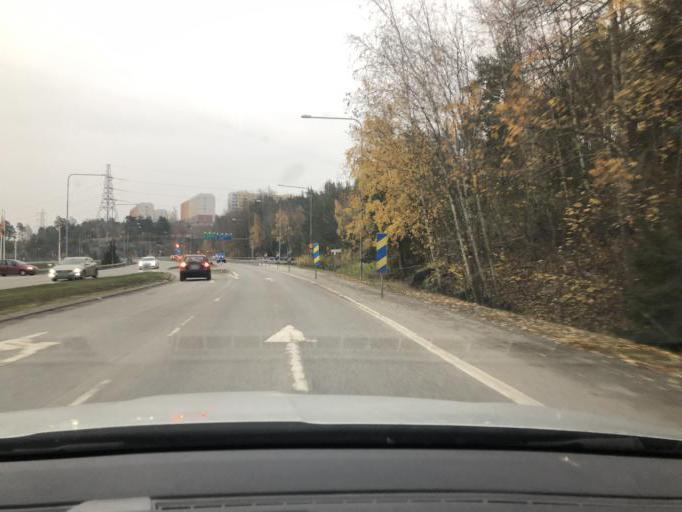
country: SE
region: Stockholm
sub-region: Botkyrka Kommun
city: Eriksberg
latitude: 59.2432
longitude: 17.8329
